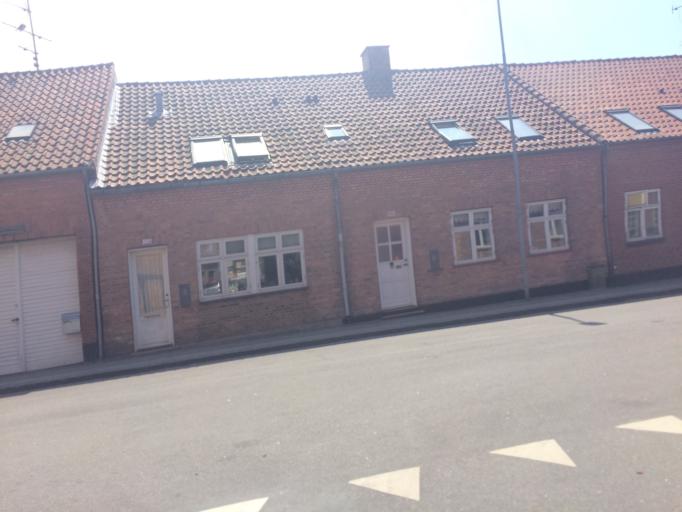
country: DK
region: Capital Region
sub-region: Bornholm Kommune
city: Ronne
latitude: 55.1002
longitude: 14.7032
